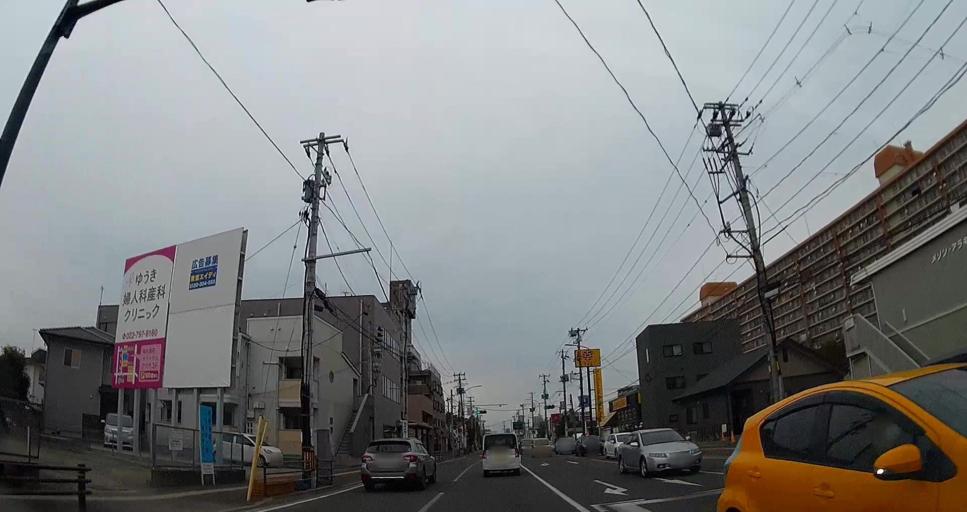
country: JP
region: Miyagi
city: Sendai
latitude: 38.2265
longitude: 140.8955
